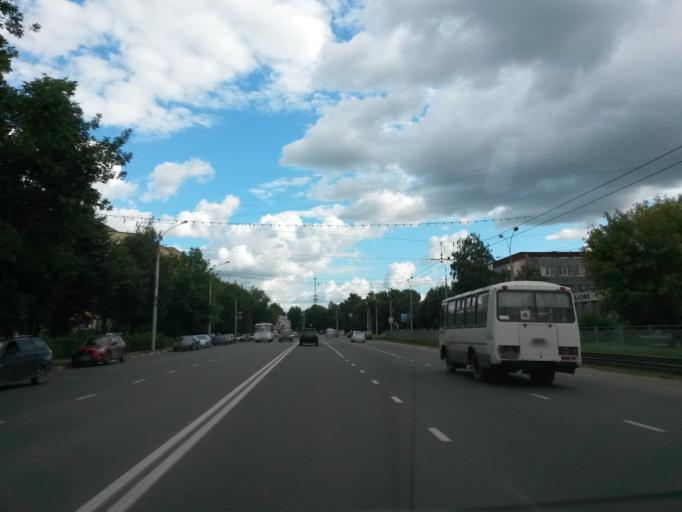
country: RU
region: Jaroslavl
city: Yaroslavl
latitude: 57.6390
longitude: 39.8578
